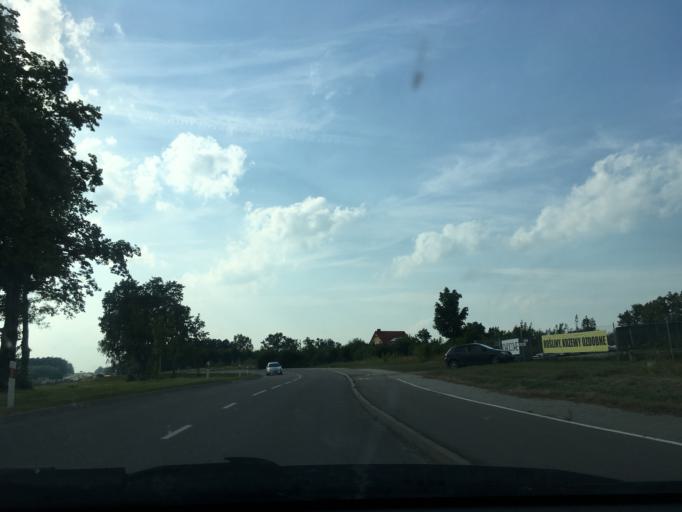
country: PL
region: Podlasie
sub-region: Powiat bialostocki
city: Choroszcz
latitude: 53.1525
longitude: 23.0381
